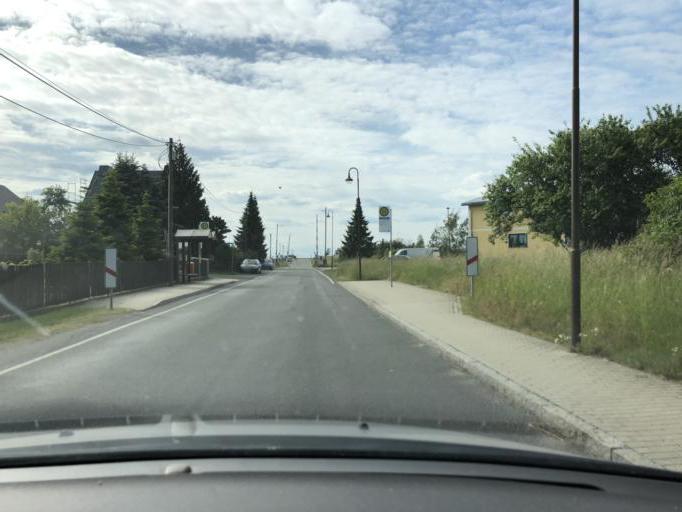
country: DE
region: Saxony
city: Grimma
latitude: 51.2760
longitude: 12.7086
